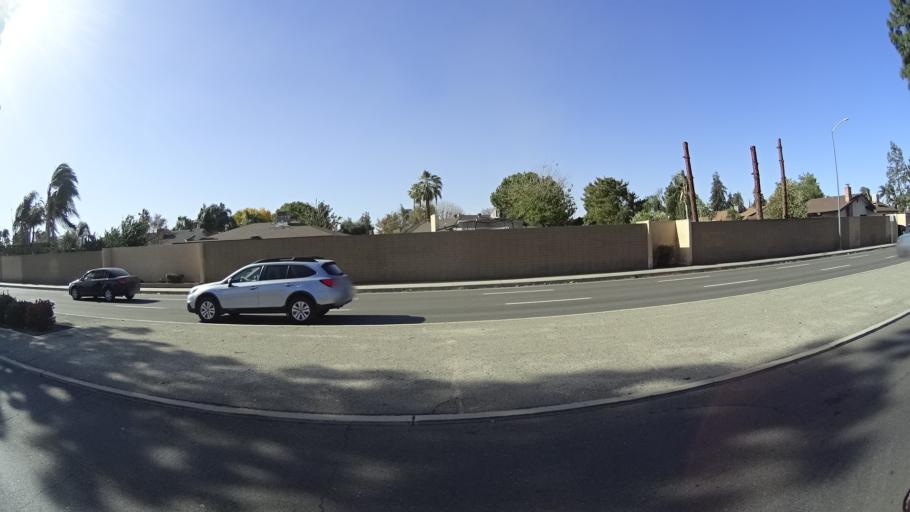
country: US
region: California
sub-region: Kern County
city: Bakersfield
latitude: 35.3334
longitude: -119.0586
